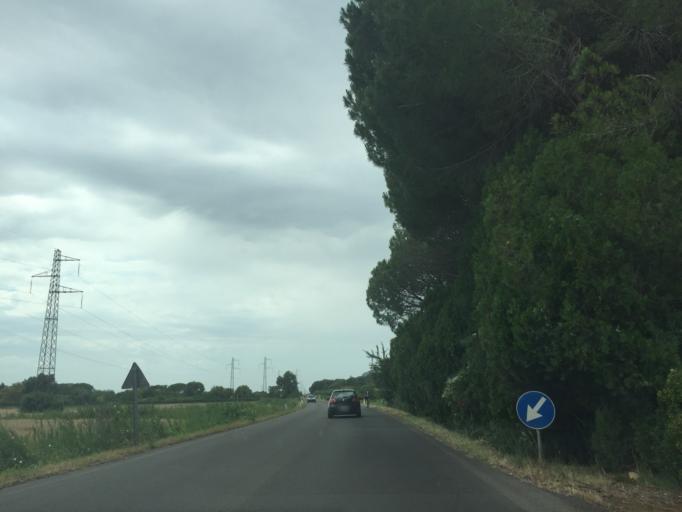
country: IT
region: Tuscany
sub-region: Province of Pisa
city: Gabella
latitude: 43.7289
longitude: 10.4854
